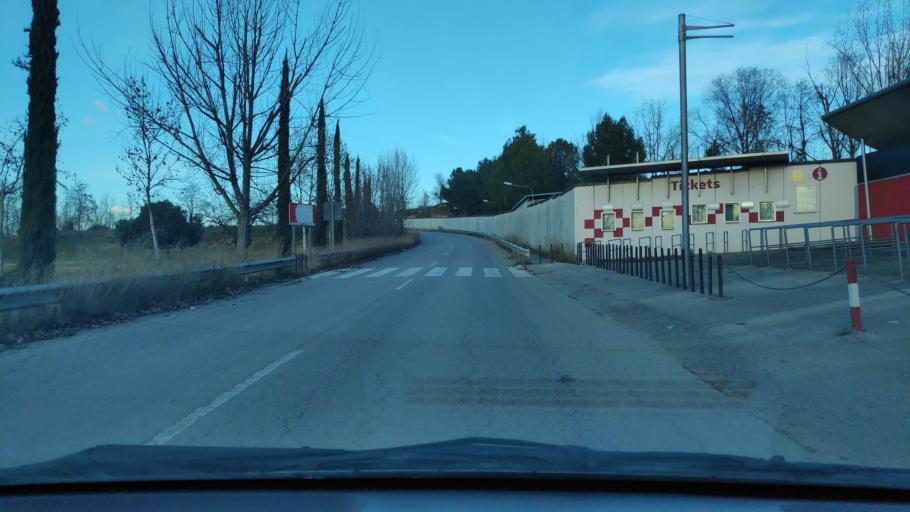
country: ES
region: Catalonia
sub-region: Provincia de Barcelona
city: Parets del Valles
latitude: 41.5692
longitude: 2.2538
